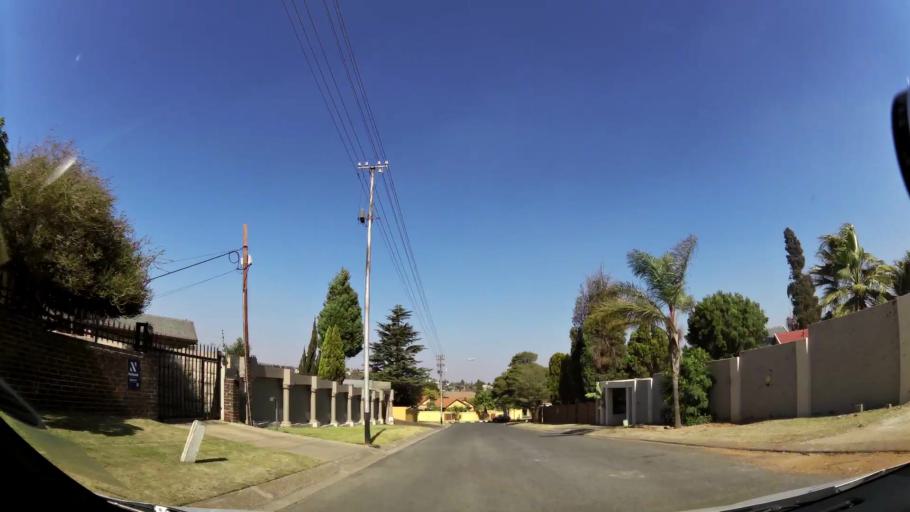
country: ZA
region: Gauteng
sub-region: City of Johannesburg Metropolitan Municipality
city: Johannesburg
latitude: -26.2668
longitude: 28.0359
